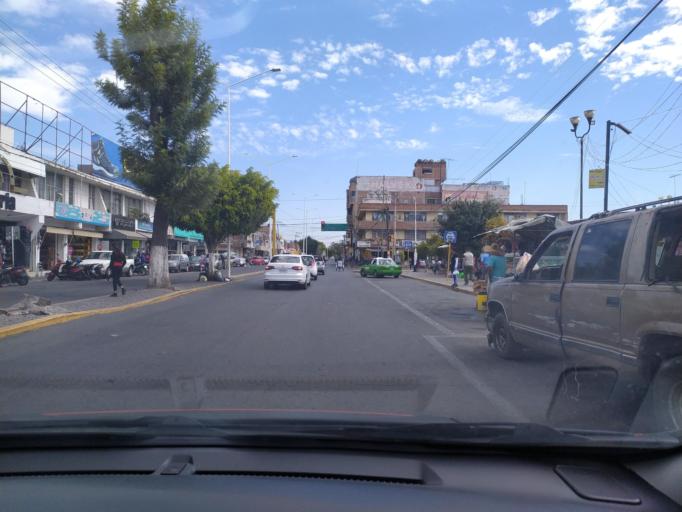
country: LA
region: Oudomxai
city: Muang La
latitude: 21.0152
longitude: 101.8583
